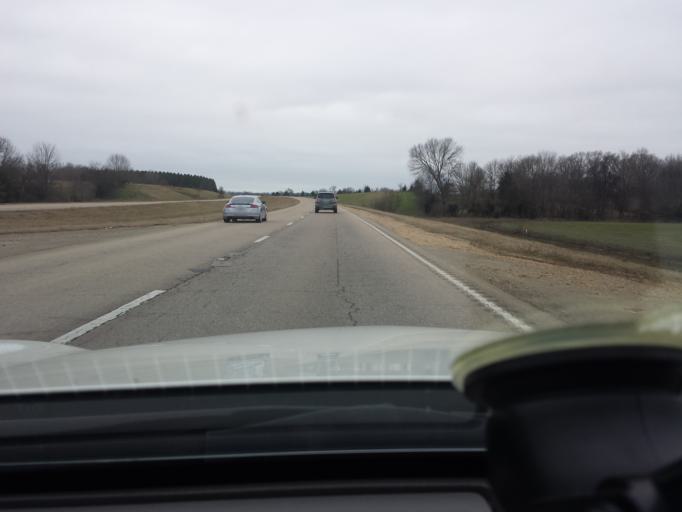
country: US
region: Mississippi
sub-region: Lee County
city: Shannon
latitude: 34.0740
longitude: -88.7029
